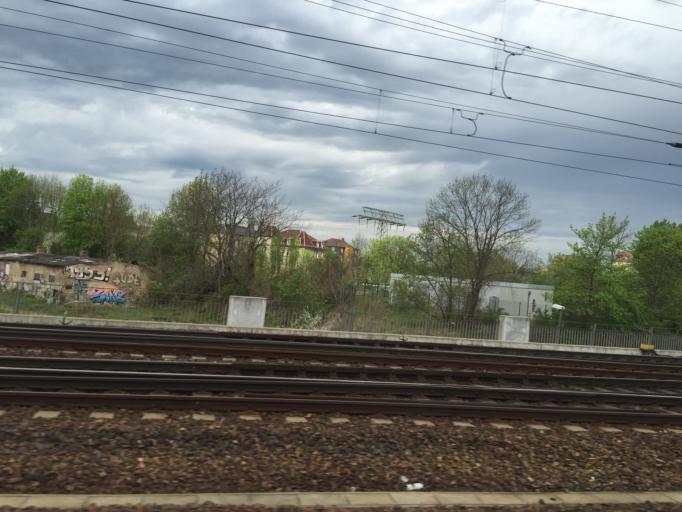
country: DE
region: Saxony
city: Dresden
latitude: 51.0501
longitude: 13.7195
